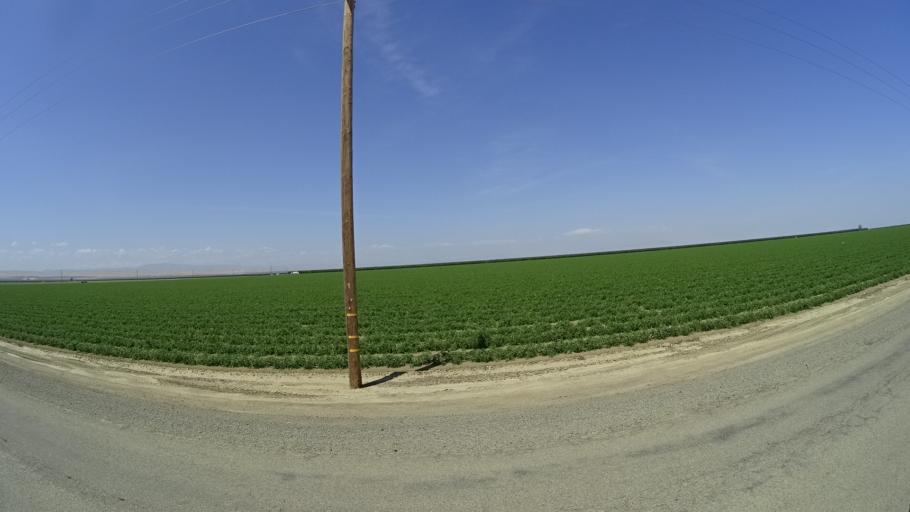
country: US
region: California
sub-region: Kings County
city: Kettleman City
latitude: 36.1260
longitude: -120.0037
